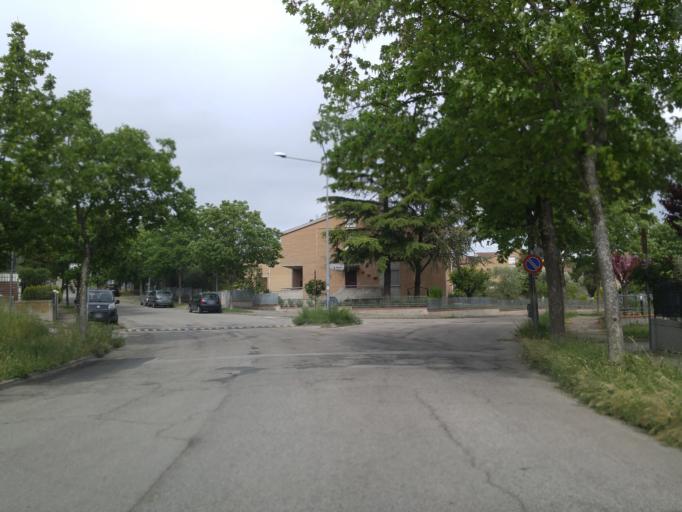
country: IT
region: The Marches
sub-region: Provincia di Pesaro e Urbino
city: Fossombrone
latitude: 43.6945
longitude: 12.8190
